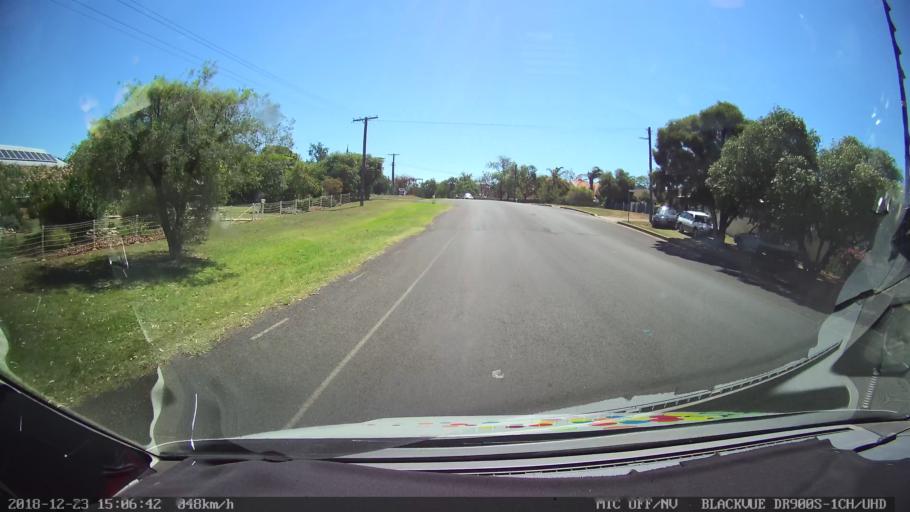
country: AU
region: New South Wales
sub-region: Tamworth Municipality
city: Manilla
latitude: -30.7459
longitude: 150.7266
